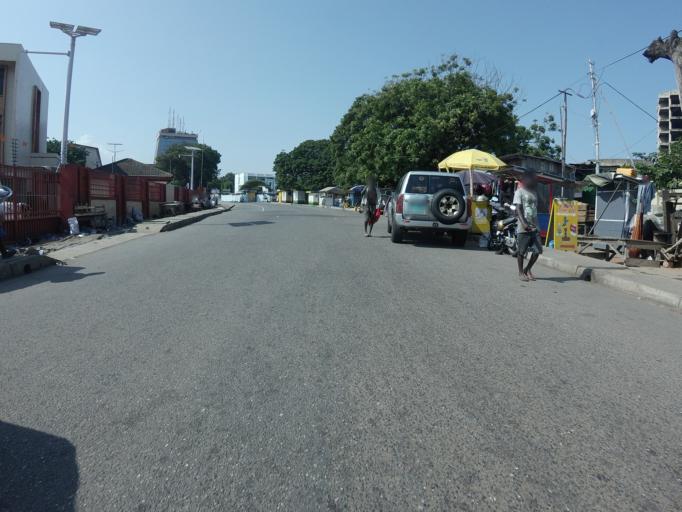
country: GH
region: Greater Accra
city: Accra
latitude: 5.5492
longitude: -0.1998
